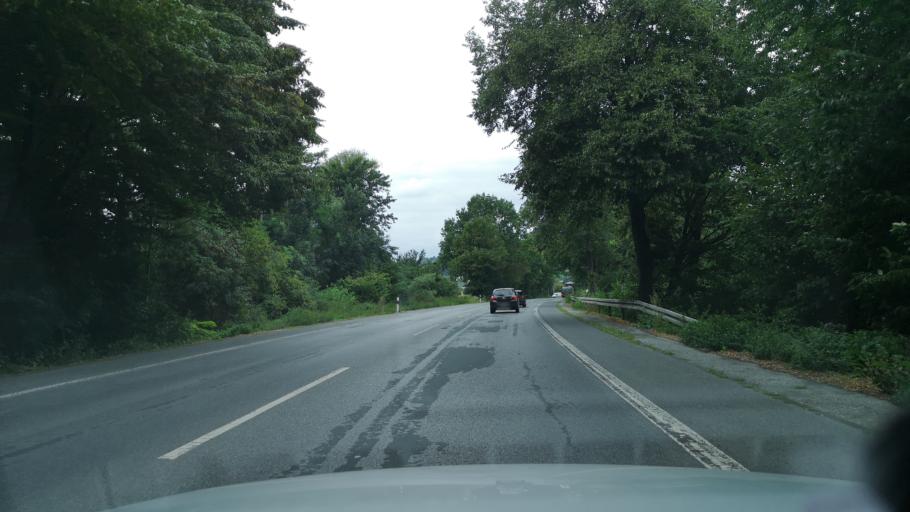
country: DE
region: North Rhine-Westphalia
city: Schwerte
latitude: 51.4093
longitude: 7.5175
